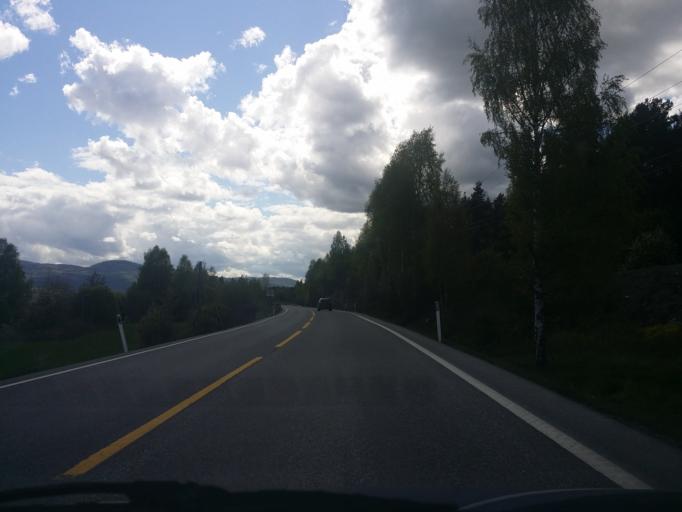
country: NO
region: Buskerud
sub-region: Modum
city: Vikersund
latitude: 59.9631
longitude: 9.9802
